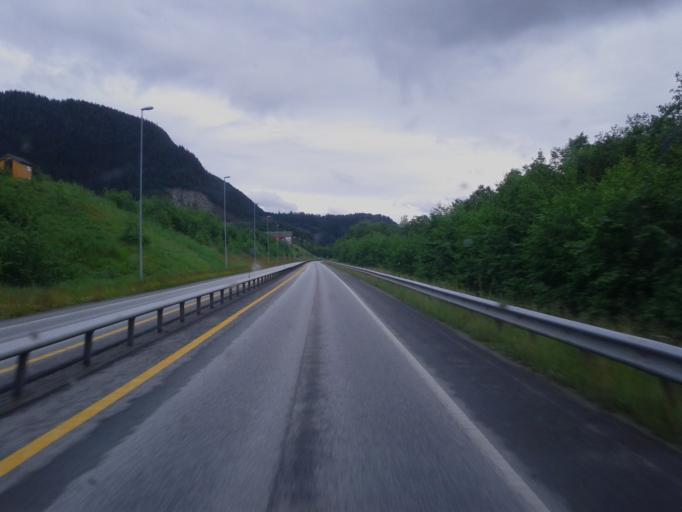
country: NO
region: Sor-Trondelag
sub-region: Melhus
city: Melhus
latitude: 63.2680
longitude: 10.2858
